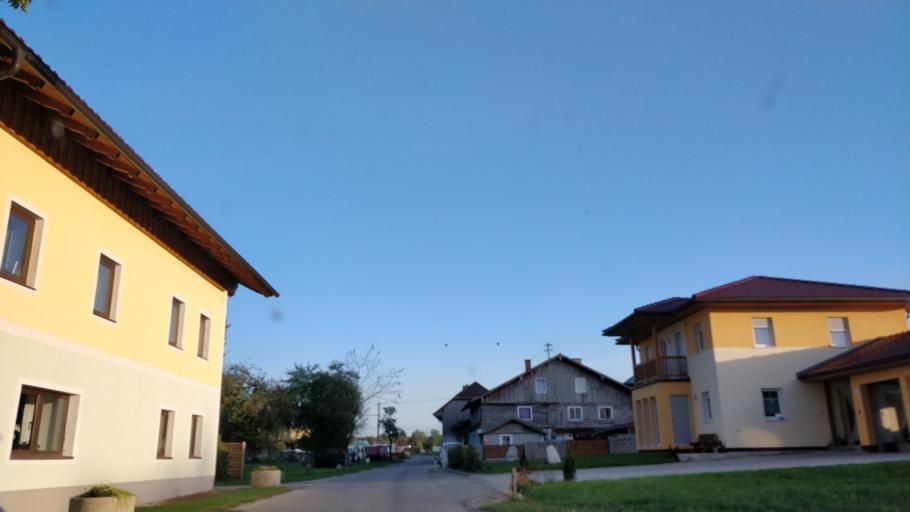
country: AT
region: Upper Austria
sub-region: Politischer Bezirk Braunau am Inn
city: Braunau am Inn
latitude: 48.1645
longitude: 13.1284
